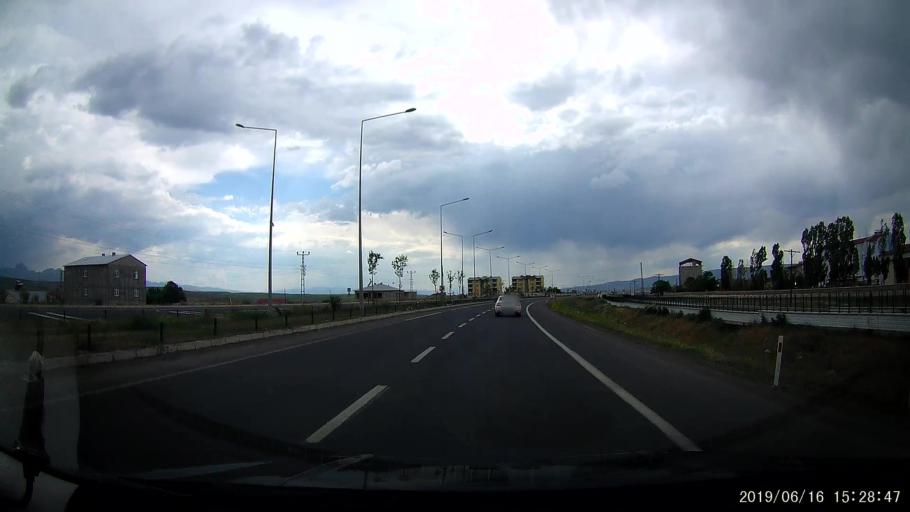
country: TR
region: Erzurum
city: Horasan
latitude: 40.0316
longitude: 42.1456
